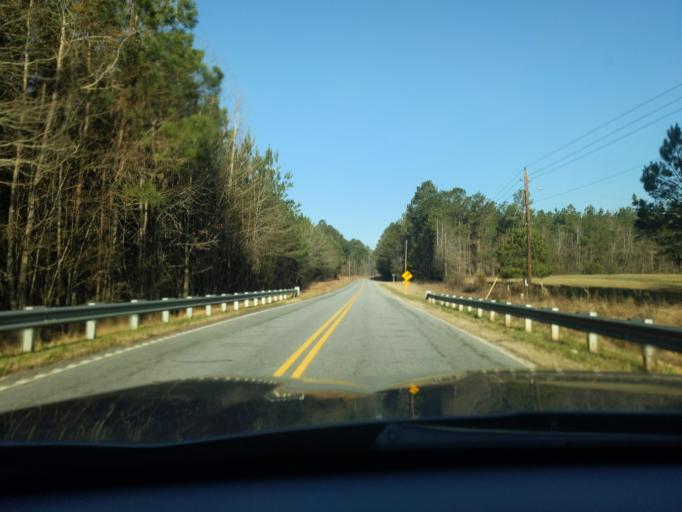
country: US
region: South Carolina
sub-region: Greenwood County
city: Ninety Six
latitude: 34.1760
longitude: -82.0926
